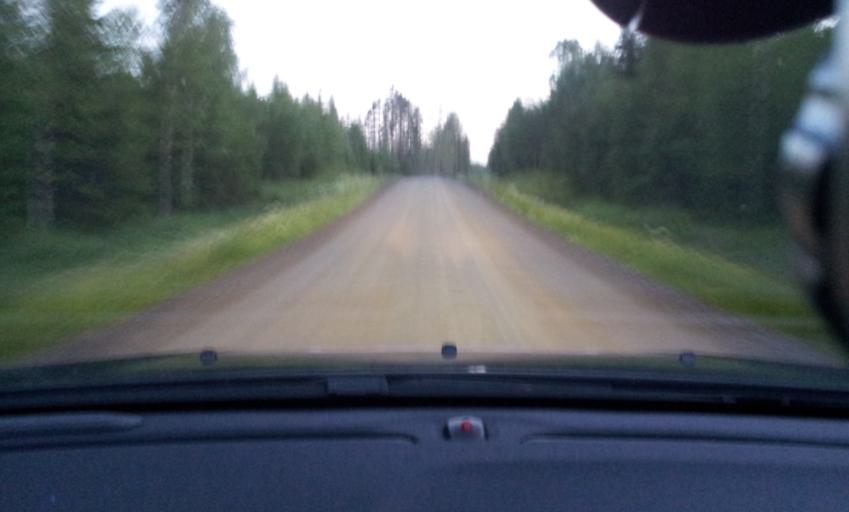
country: SE
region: Vaesternorrland
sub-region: Ange Kommun
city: Fransta
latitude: 62.7766
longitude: 15.9671
